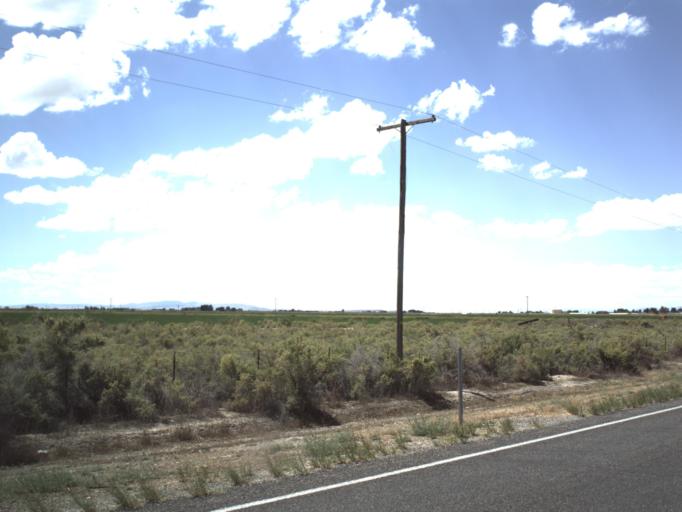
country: US
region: Utah
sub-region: Millard County
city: Delta
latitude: 39.3529
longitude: -112.5328
